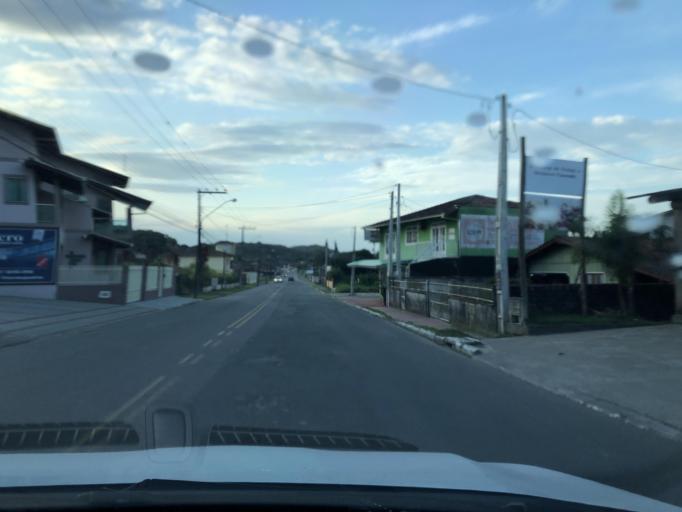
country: BR
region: Santa Catarina
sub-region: Sao Francisco Do Sul
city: Sao Francisco do Sul
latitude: -26.2547
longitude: -48.6266
